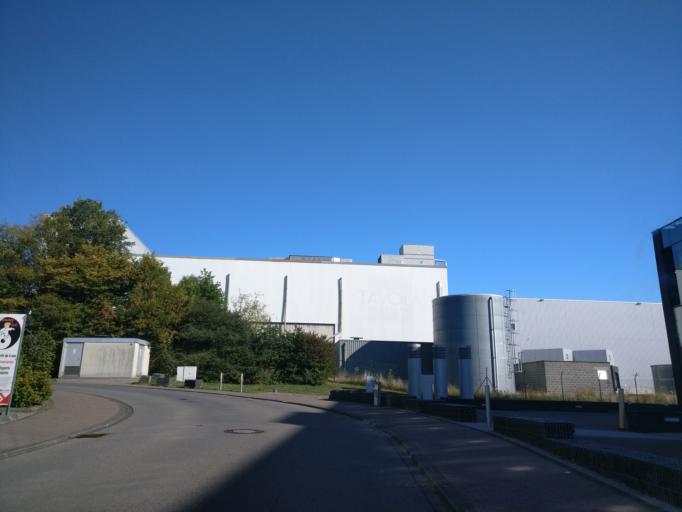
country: LU
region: Luxembourg
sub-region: Canton de Capellen
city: Mamer
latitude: 49.6405
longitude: 6.0097
